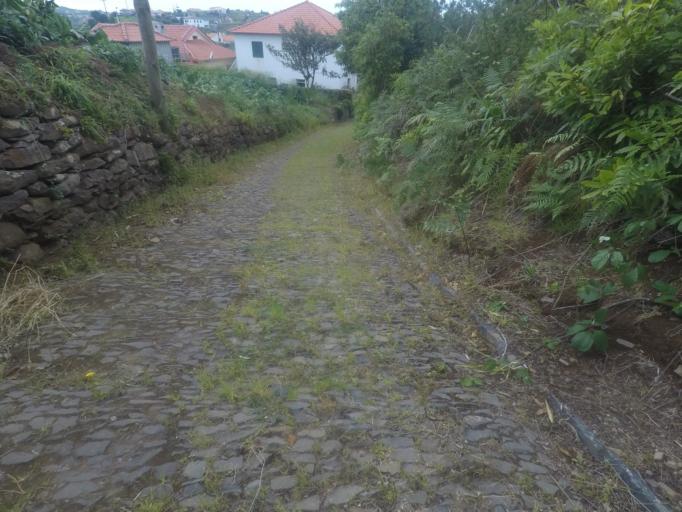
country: PT
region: Madeira
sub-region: Santana
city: Santana
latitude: 32.8222
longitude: -16.8857
